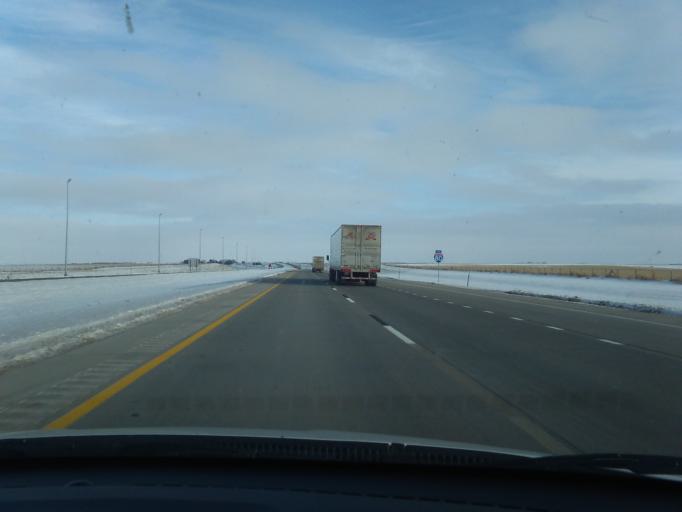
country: US
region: Nebraska
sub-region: Cheyenne County
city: Sidney
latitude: 41.1128
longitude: -102.9401
